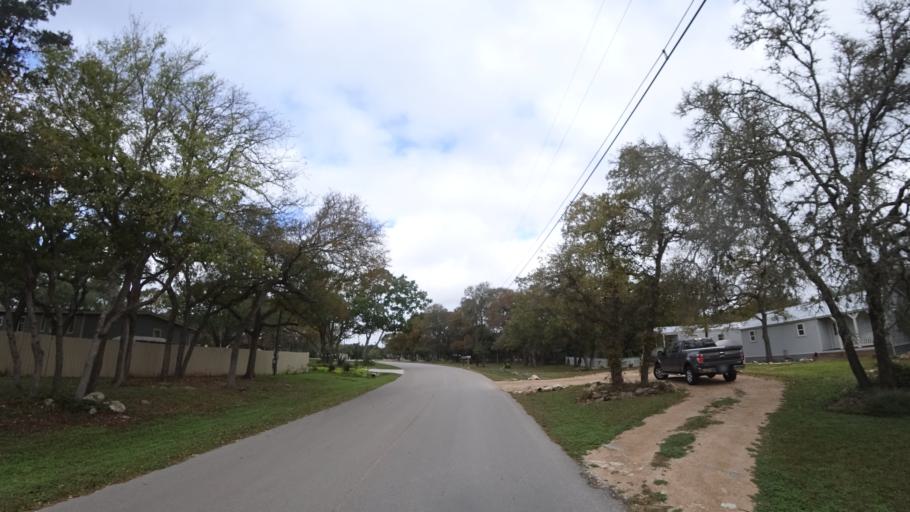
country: US
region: Texas
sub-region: Travis County
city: Bee Cave
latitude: 30.2529
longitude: -97.9210
